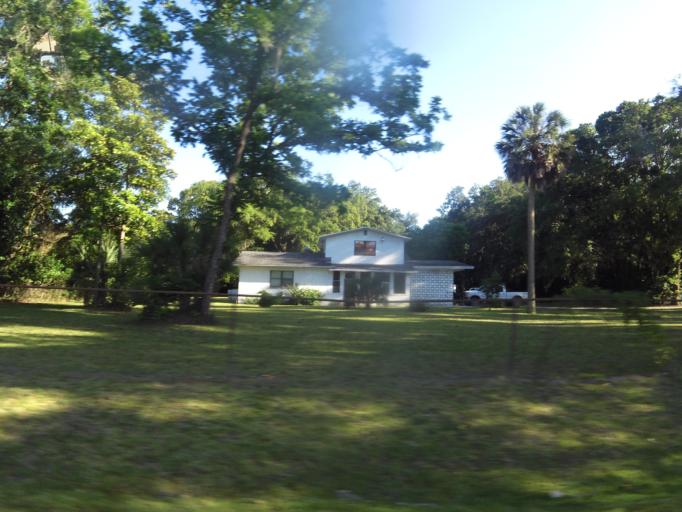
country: US
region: Florida
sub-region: Duval County
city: Jacksonville
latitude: 30.4629
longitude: -81.5661
